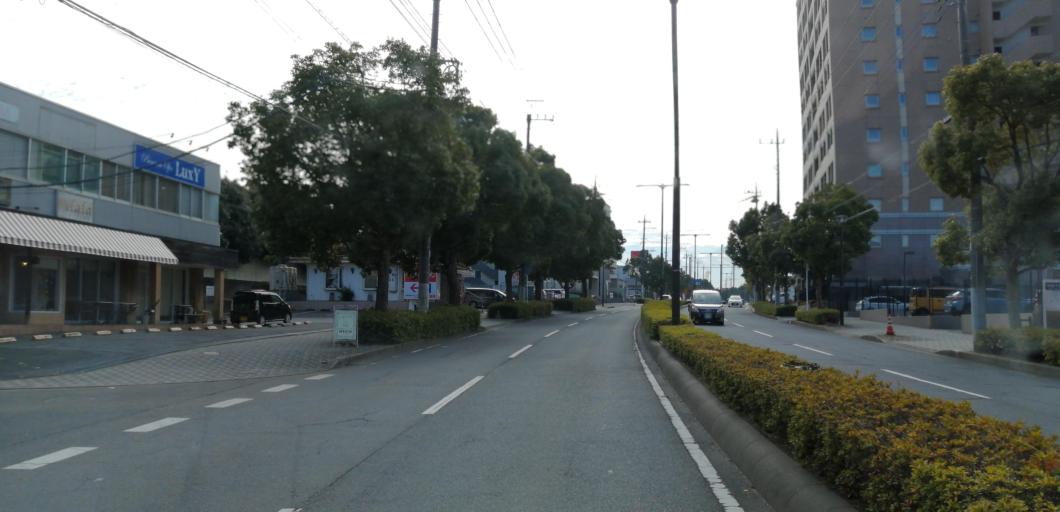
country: JP
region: Chiba
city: Narita
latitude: 35.7577
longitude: 140.2982
